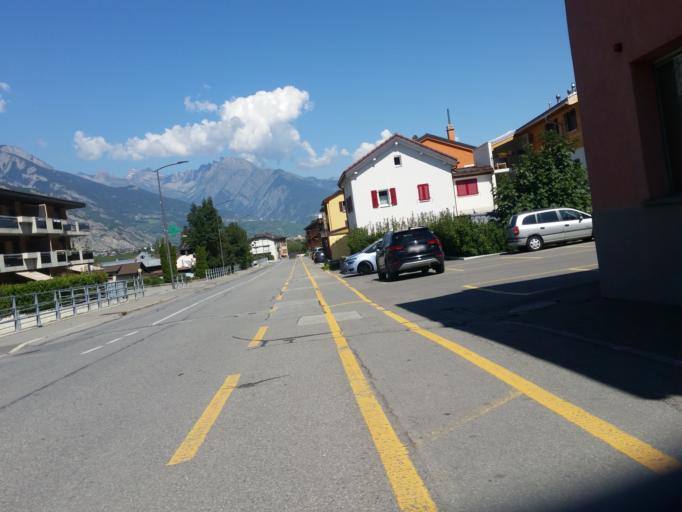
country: CH
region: Valais
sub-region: Martigny District
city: Riddes
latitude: 46.1735
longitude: 7.2230
